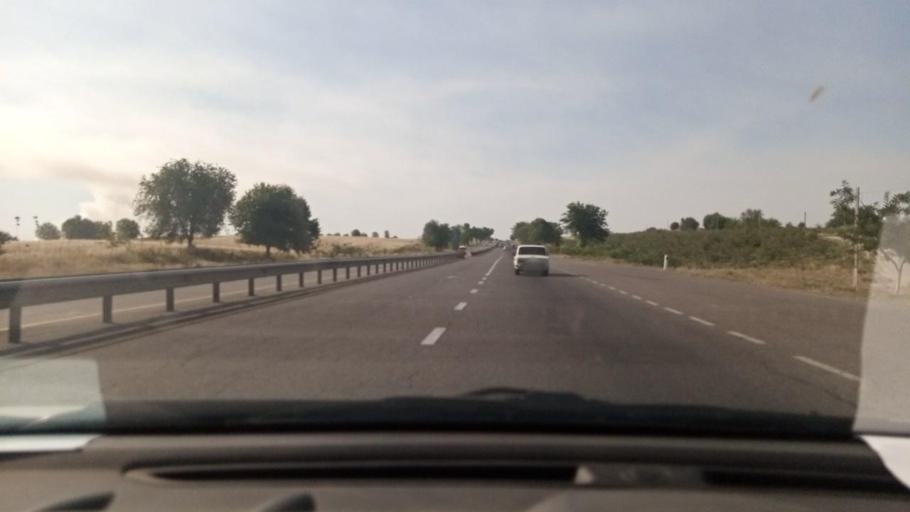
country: UZ
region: Toshkent
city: Tuytepa
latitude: 41.1146
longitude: 69.4459
